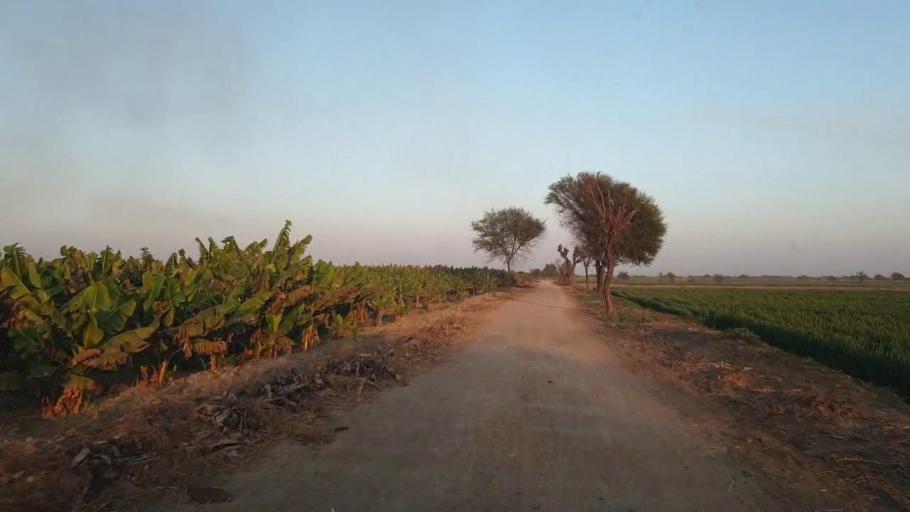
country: PK
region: Sindh
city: Tando Allahyar
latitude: 25.3629
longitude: 68.7315
